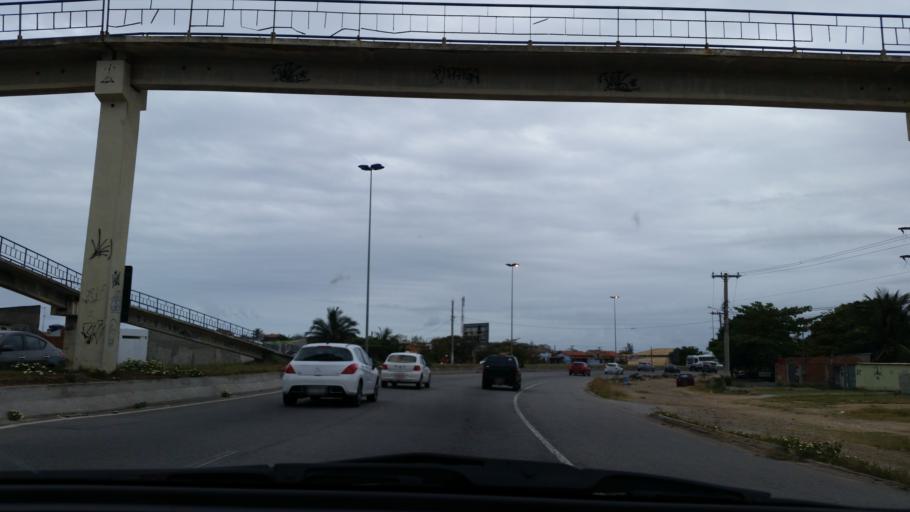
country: BR
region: Rio de Janeiro
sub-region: Cabo Frio
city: Cabo Frio
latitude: -22.8566
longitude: -42.0581
